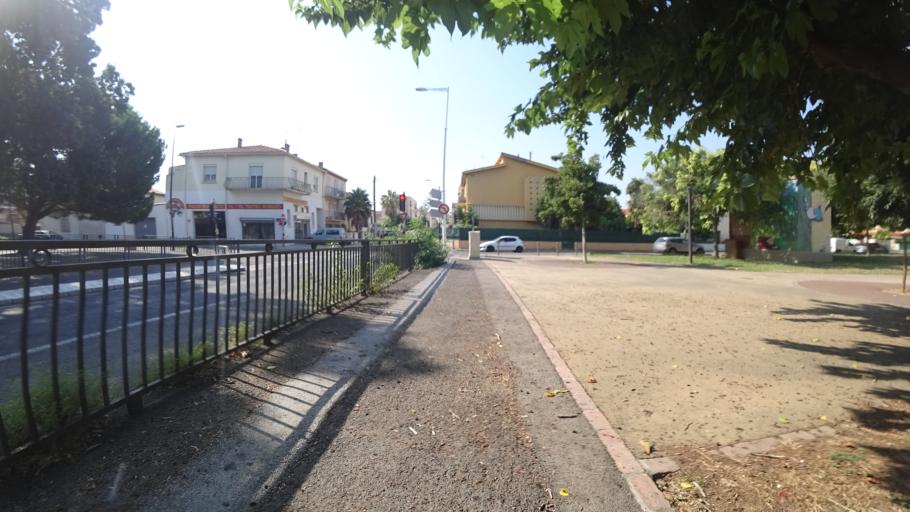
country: FR
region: Languedoc-Roussillon
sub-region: Departement des Pyrenees-Orientales
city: Perpignan
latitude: 42.7042
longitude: 2.8825
